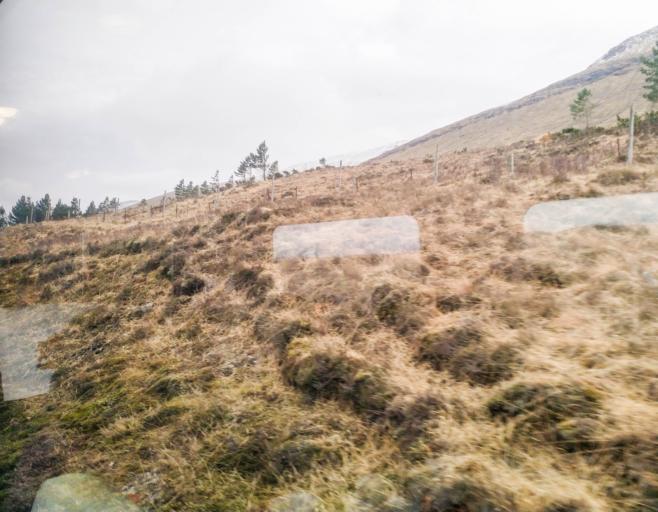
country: GB
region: Scotland
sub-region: Highland
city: Spean Bridge
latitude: 56.5628
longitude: -4.7101
